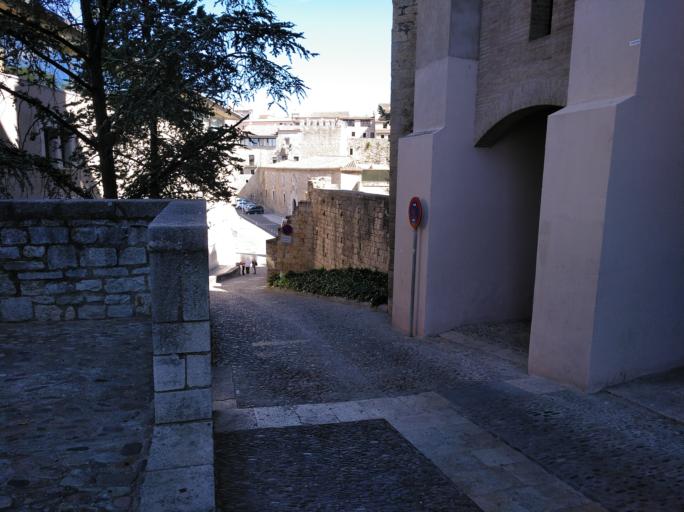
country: ES
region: Catalonia
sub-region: Provincia de Girona
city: Girona
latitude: 41.9854
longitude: 2.8276
